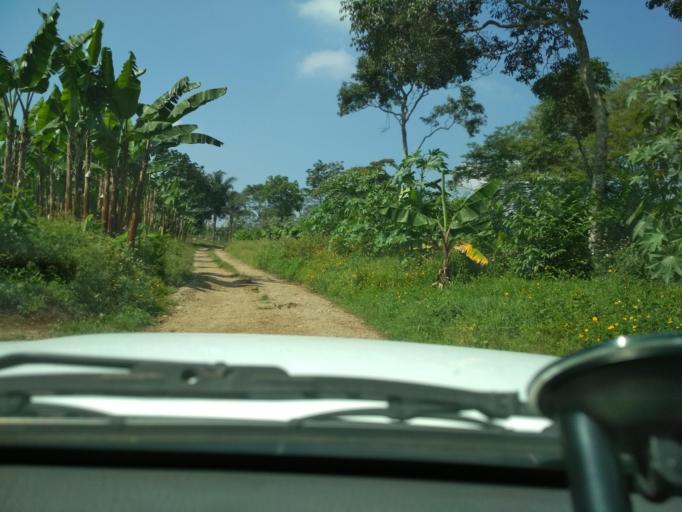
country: MX
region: Veracruz
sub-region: Fortin
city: Santa Lucia Potrerillo
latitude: 18.9781
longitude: -97.0196
